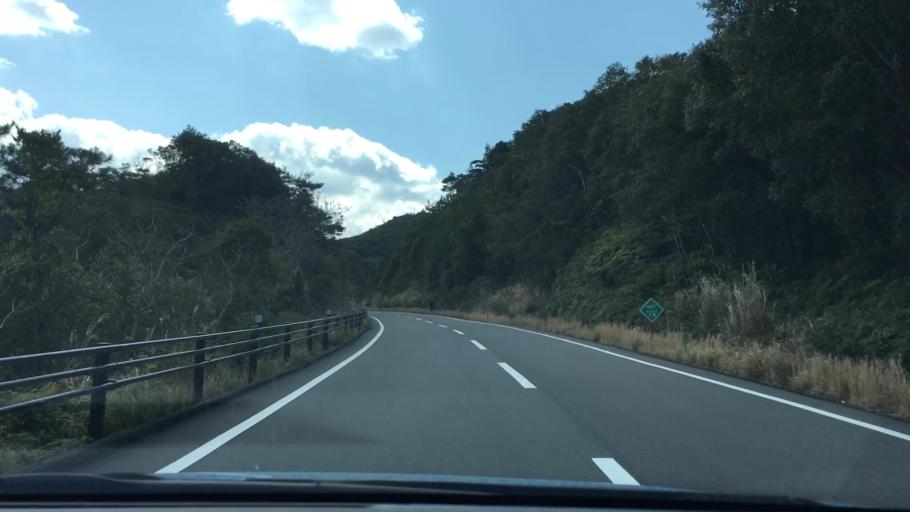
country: JP
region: Mie
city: Toba
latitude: 34.4346
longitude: 136.9124
